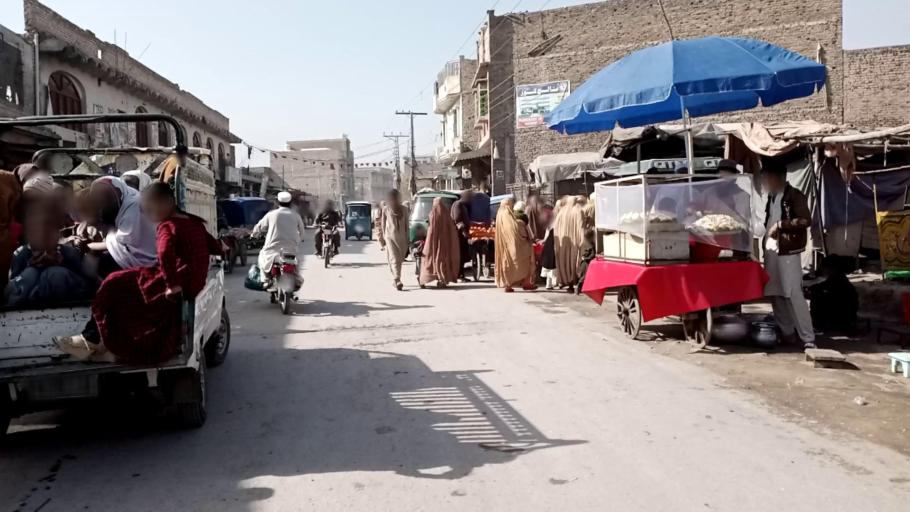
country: PK
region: Khyber Pakhtunkhwa
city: Peshawar
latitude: 33.9922
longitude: 71.5835
